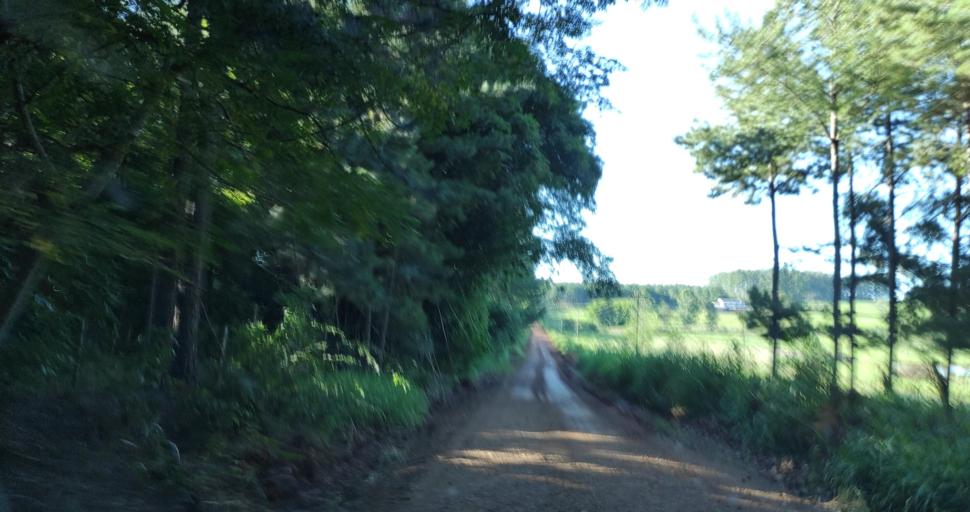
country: AR
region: Misiones
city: Puerto Rico
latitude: -26.8384
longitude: -55.0022
